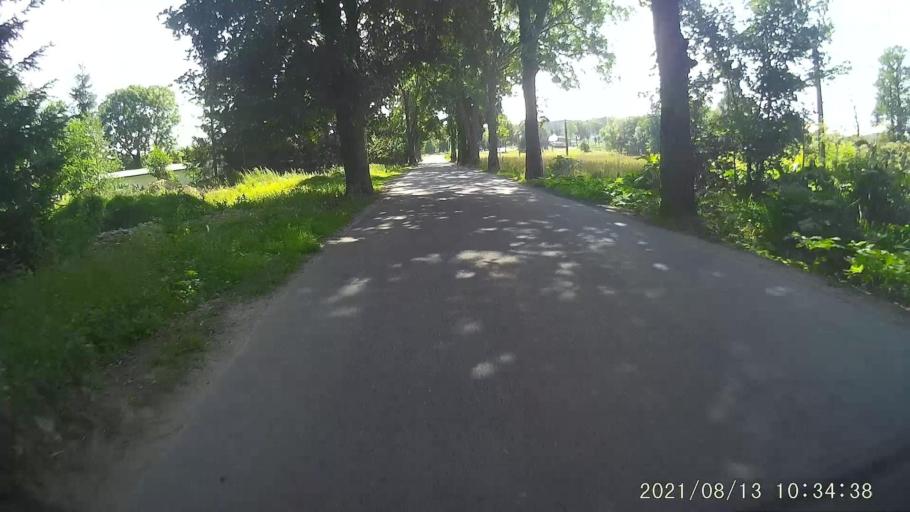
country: PL
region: Lower Silesian Voivodeship
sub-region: Powiat klodzki
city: Duszniki-Zdroj
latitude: 50.4264
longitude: 16.3713
